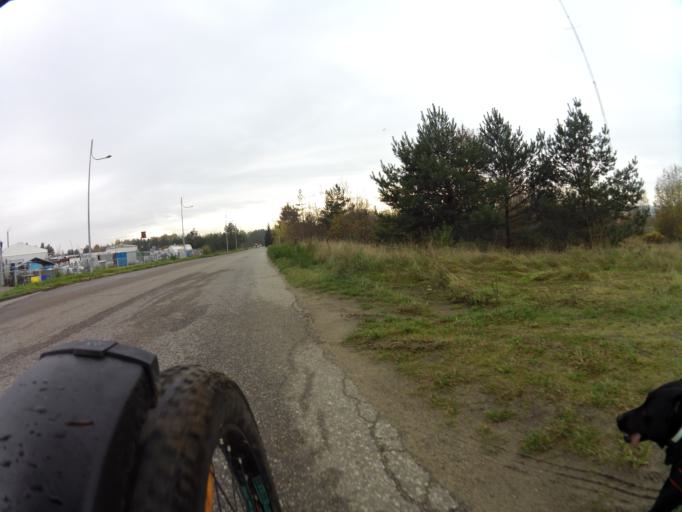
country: PL
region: Pomeranian Voivodeship
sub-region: Powiat pucki
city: Krokowa
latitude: 54.7377
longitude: 18.0939
